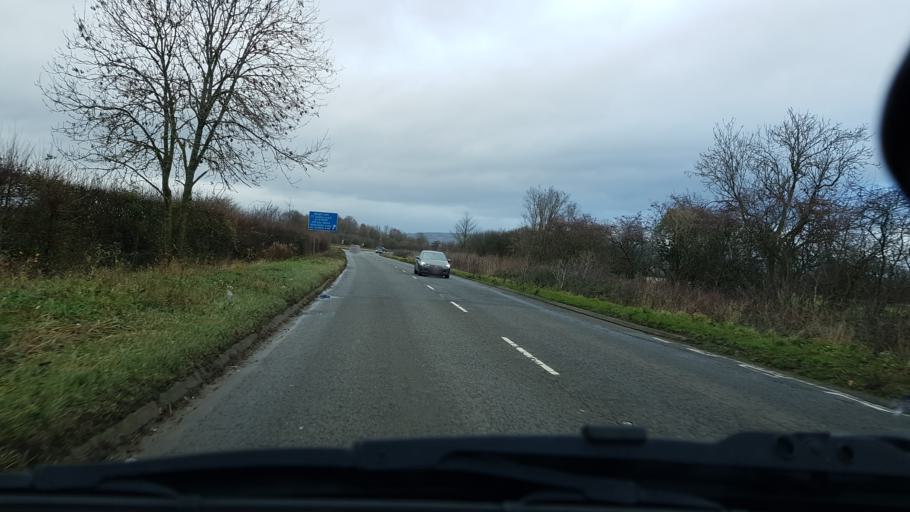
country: GB
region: England
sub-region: Gloucestershire
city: Gotherington
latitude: 51.9823
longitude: -2.0719
